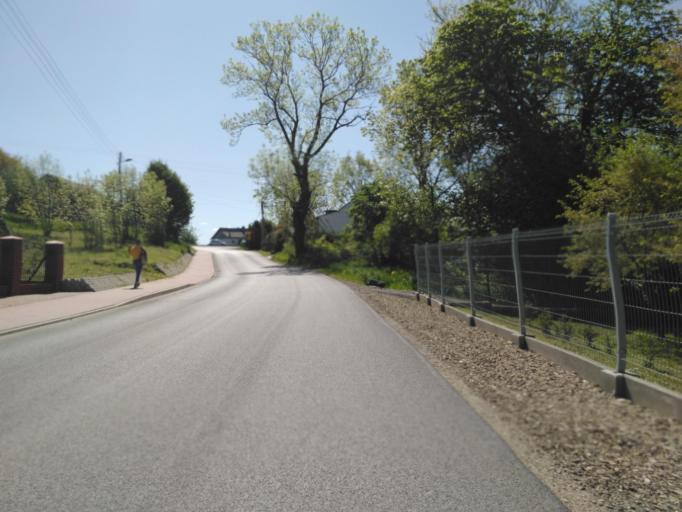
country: PL
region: Subcarpathian Voivodeship
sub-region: Powiat krosnienski
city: Miejsce Piastowe
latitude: 49.6463
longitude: 21.8072
